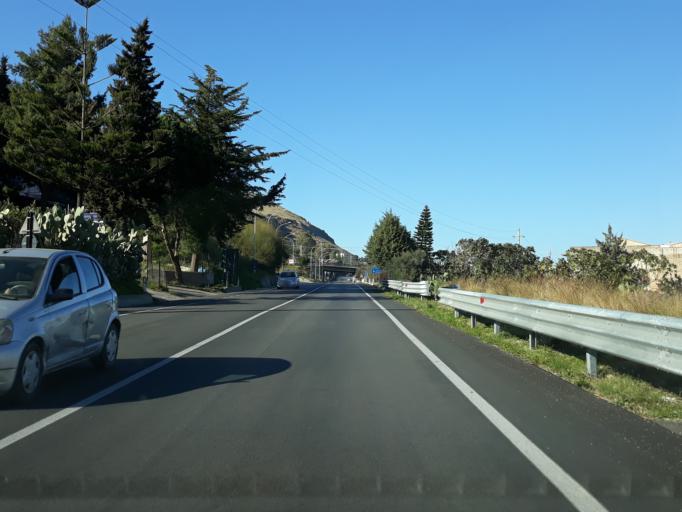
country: IT
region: Sicily
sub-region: Palermo
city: Misilmeri
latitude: 38.0407
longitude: 13.4610
